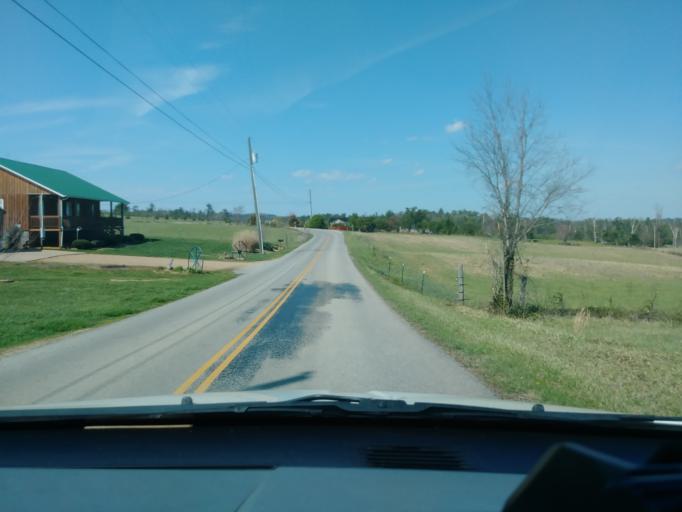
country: US
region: Tennessee
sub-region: Greene County
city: Tusculum
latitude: 36.0667
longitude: -82.7755
